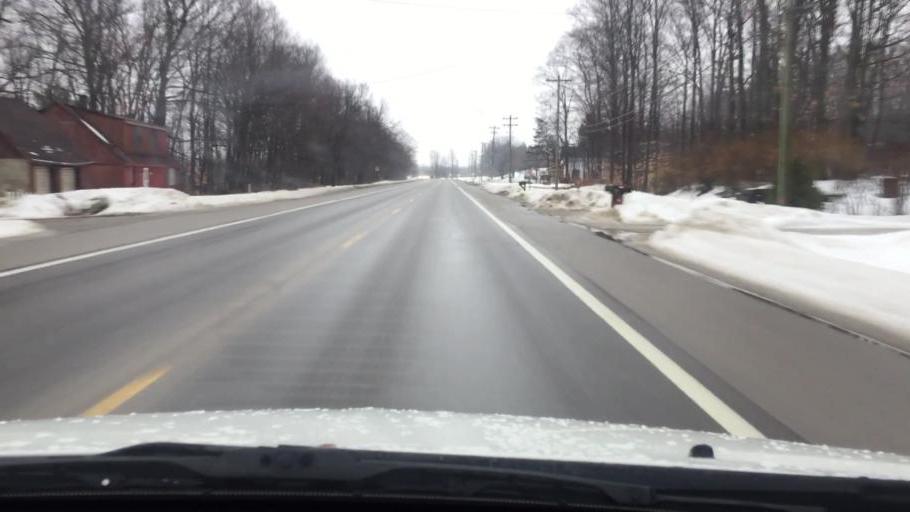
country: US
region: Michigan
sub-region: Charlevoix County
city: Charlevoix
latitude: 45.2873
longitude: -85.2442
